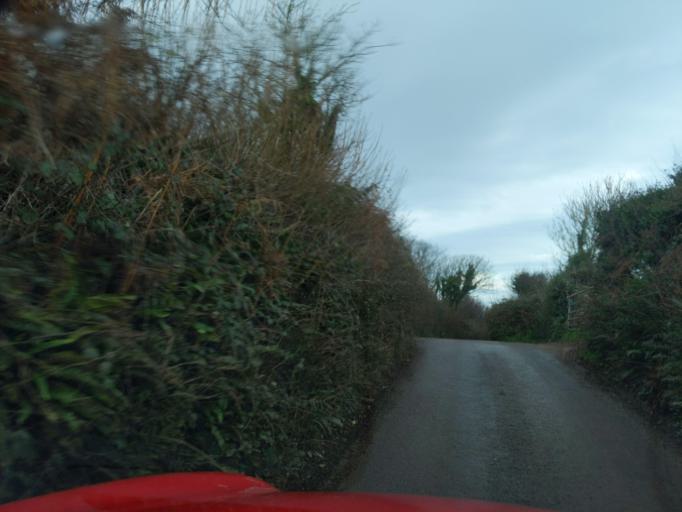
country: GB
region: England
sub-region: Devon
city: Salcombe
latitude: 50.2516
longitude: -3.6686
